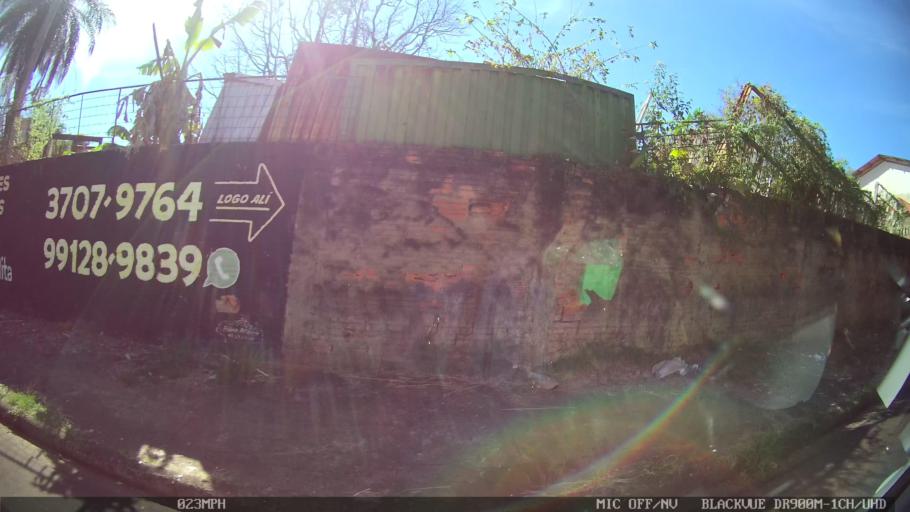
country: BR
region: Sao Paulo
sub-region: Franca
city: Franca
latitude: -20.5448
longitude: -47.3910
